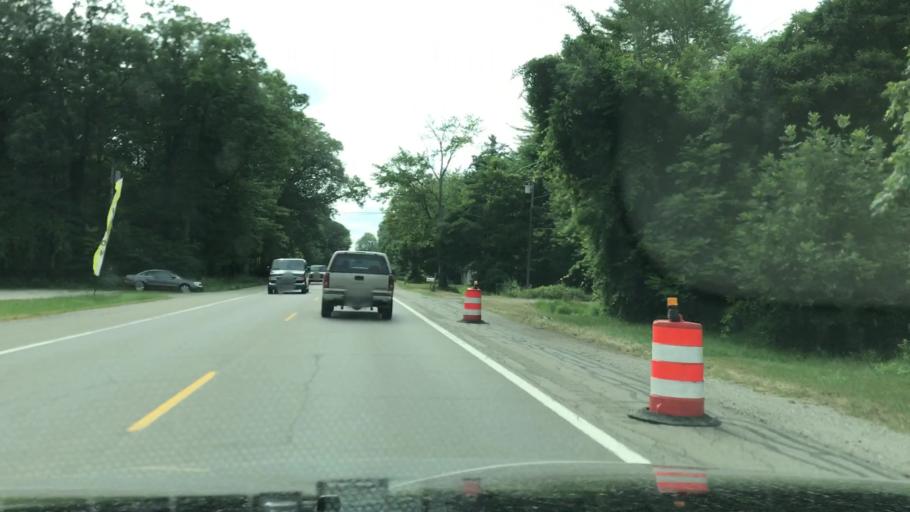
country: US
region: Michigan
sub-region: Muskegon County
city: Fruitport
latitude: 43.0739
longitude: -86.1279
